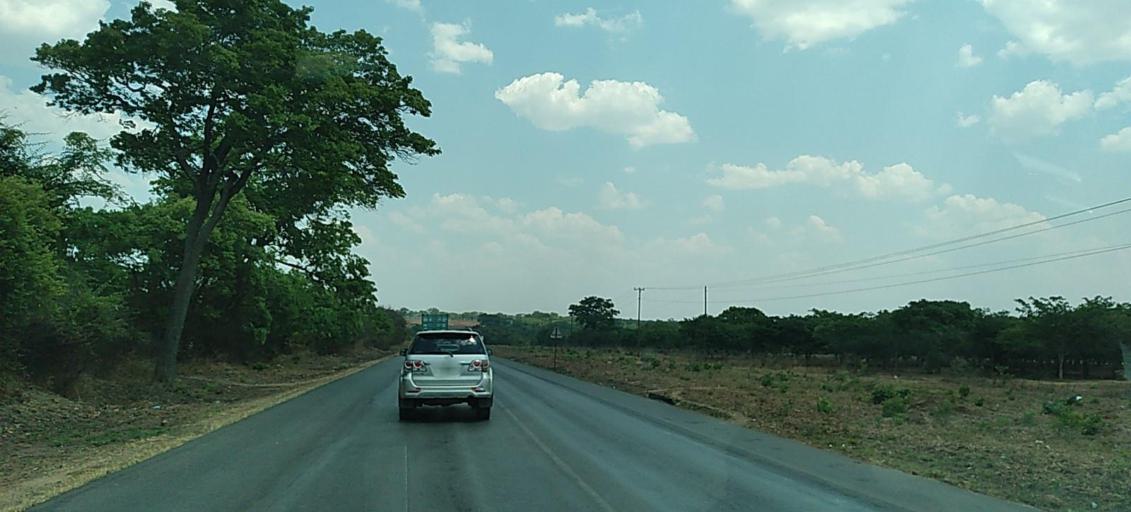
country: ZM
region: Central
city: Kabwe
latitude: -14.3123
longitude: 28.5455
